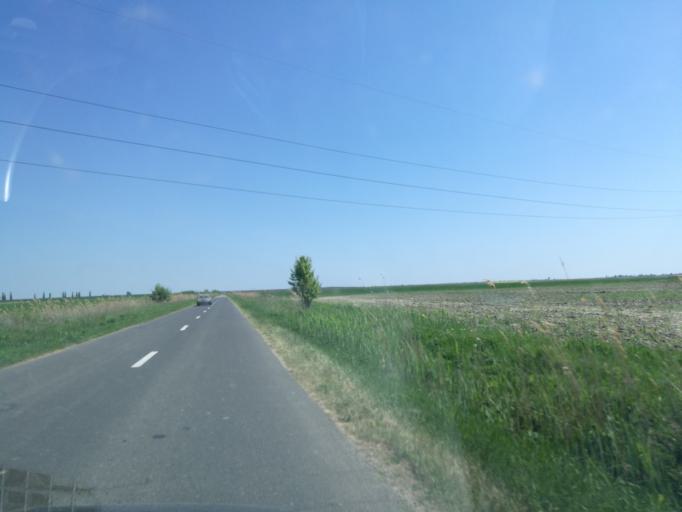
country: RO
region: Ialomita
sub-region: Comuna Adancata
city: Adancata
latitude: 44.7816
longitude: 26.4528
